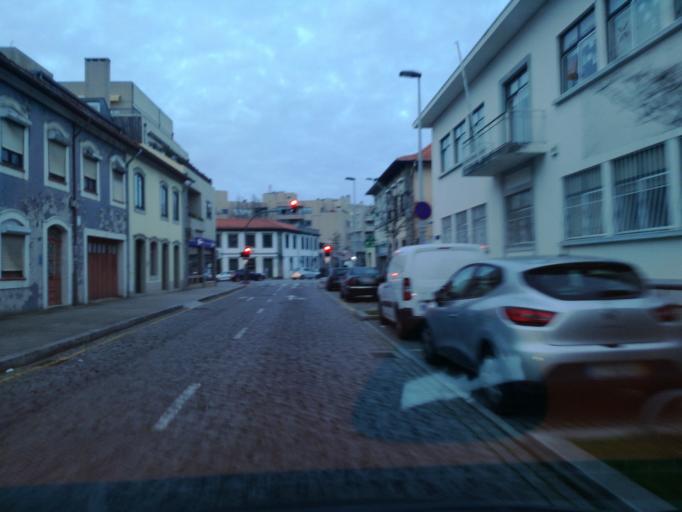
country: PT
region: Porto
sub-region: Vila Nova de Gaia
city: Canidelo
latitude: 41.1535
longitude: -8.6484
